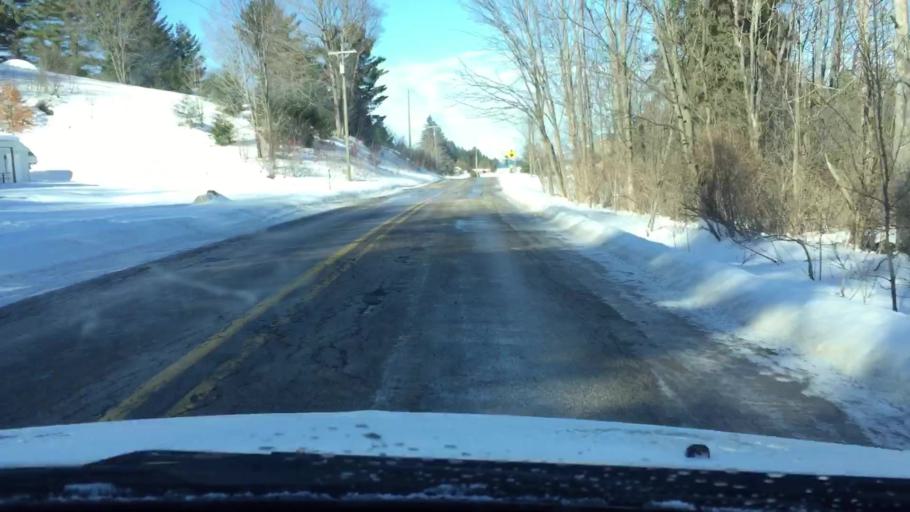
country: US
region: Michigan
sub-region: Charlevoix County
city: East Jordan
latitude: 45.1096
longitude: -85.1292
